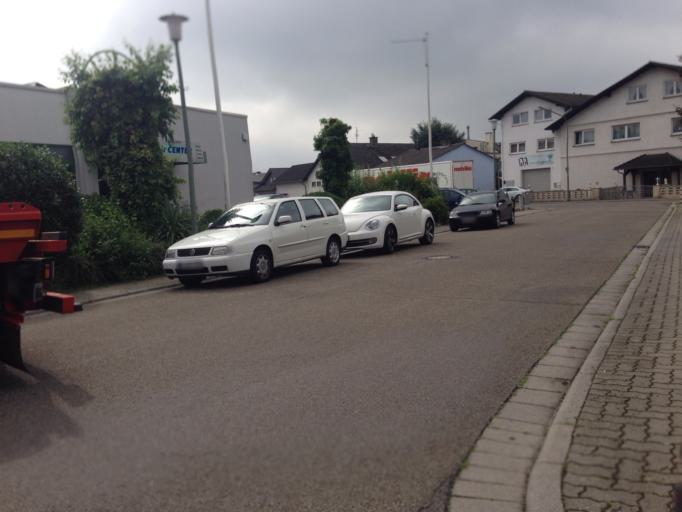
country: DE
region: Hesse
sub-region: Regierungsbezirk Darmstadt
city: Hanau am Main
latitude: 50.1021
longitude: 8.9151
